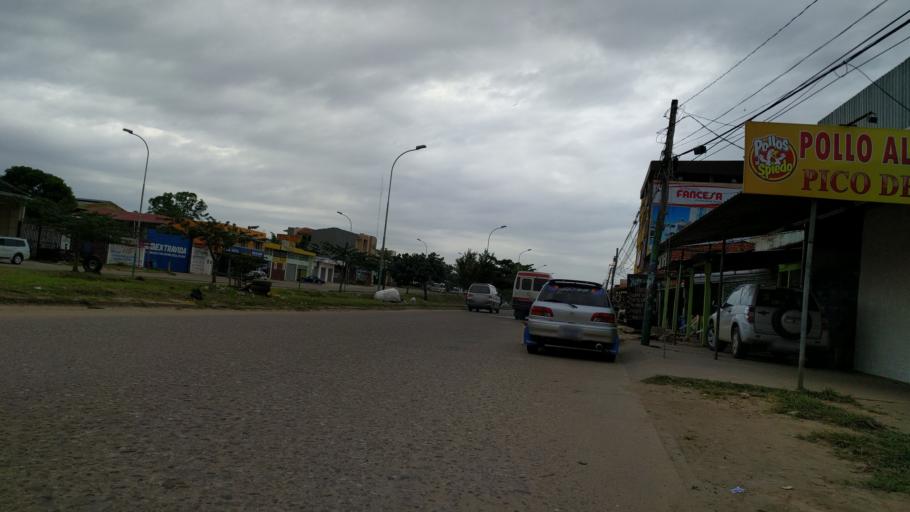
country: BO
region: Santa Cruz
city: Santa Cruz de la Sierra
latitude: -17.8117
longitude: -63.2192
